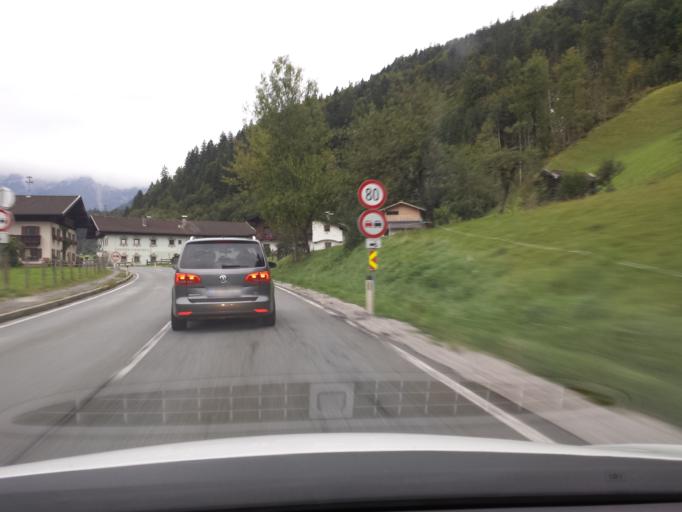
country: AT
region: Salzburg
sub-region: Politischer Bezirk Zell am See
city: Unken
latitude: 47.6168
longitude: 12.7067
